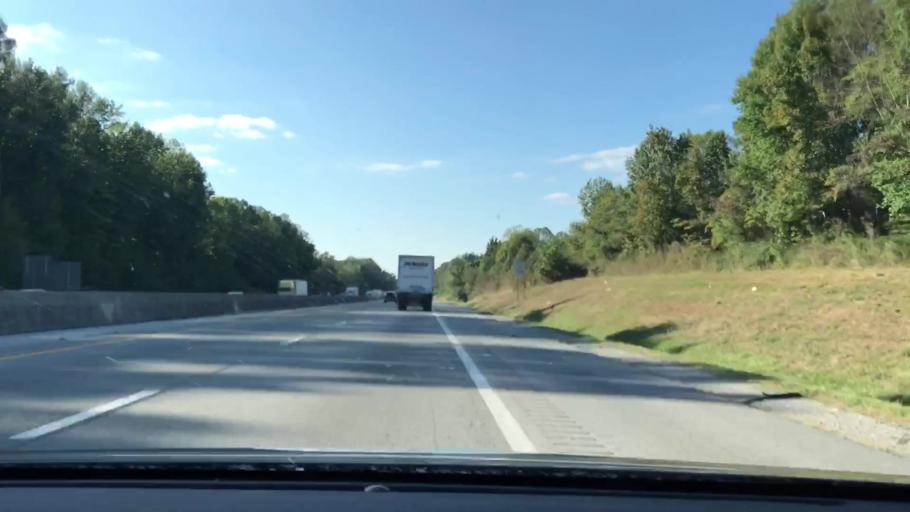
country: US
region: Tennessee
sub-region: Putnam County
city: Lafayette
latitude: 36.0936
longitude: -85.7326
